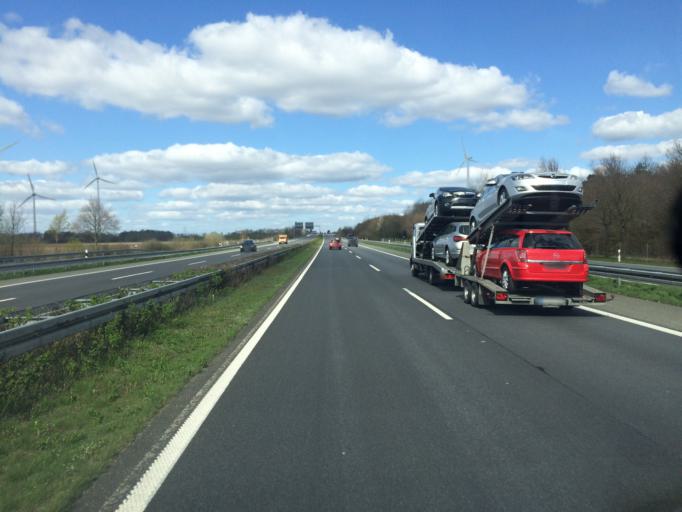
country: DE
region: North Rhine-Westphalia
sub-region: Regierungsbezirk Munster
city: Ochtrup
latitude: 52.1945
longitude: 7.1174
